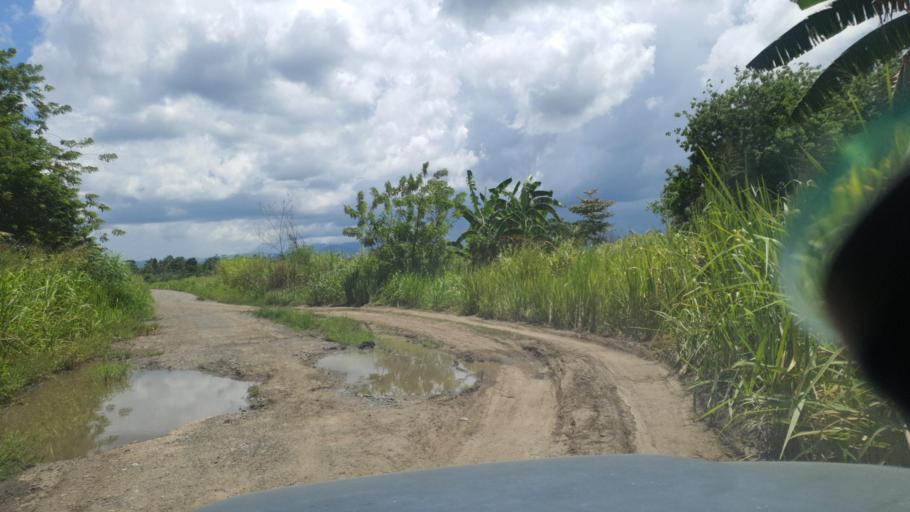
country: SB
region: Guadalcanal
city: Honiara
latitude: -9.4369
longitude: 160.1502
